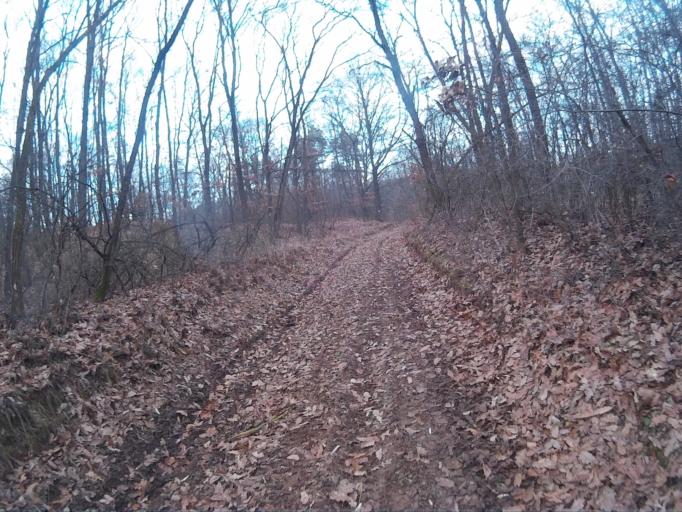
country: HU
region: Nograd
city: Rimoc
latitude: 47.9976
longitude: 19.4303
